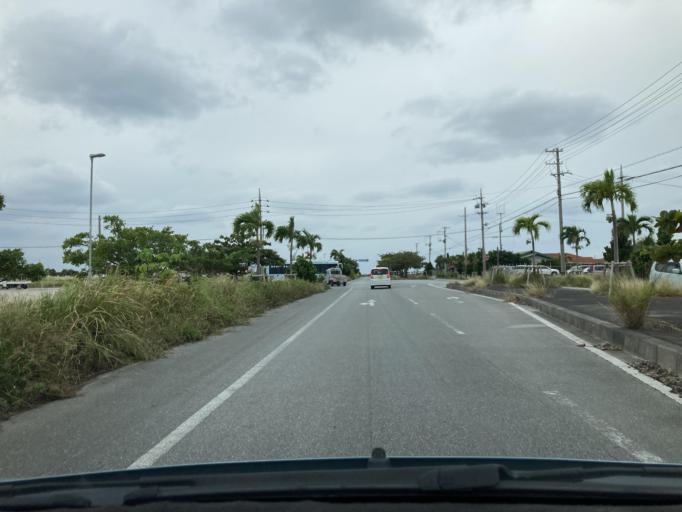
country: JP
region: Okinawa
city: Itoman
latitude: 26.1358
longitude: 127.6534
